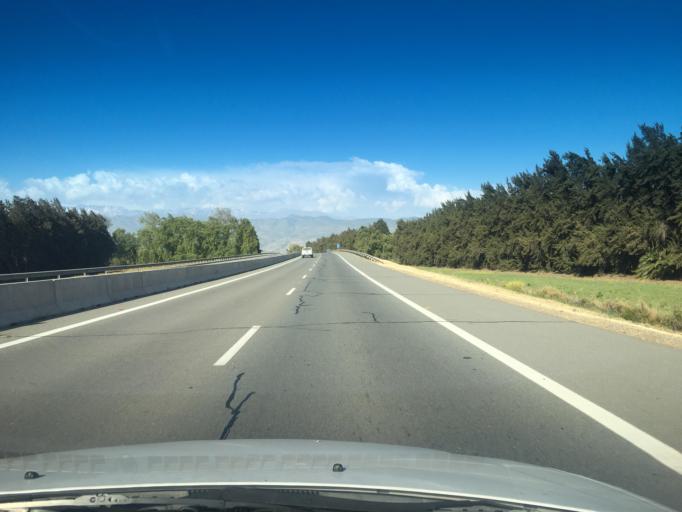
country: CL
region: Santiago Metropolitan
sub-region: Provincia de Chacabuco
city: Chicureo Abajo
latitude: -33.2939
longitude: -70.7152
